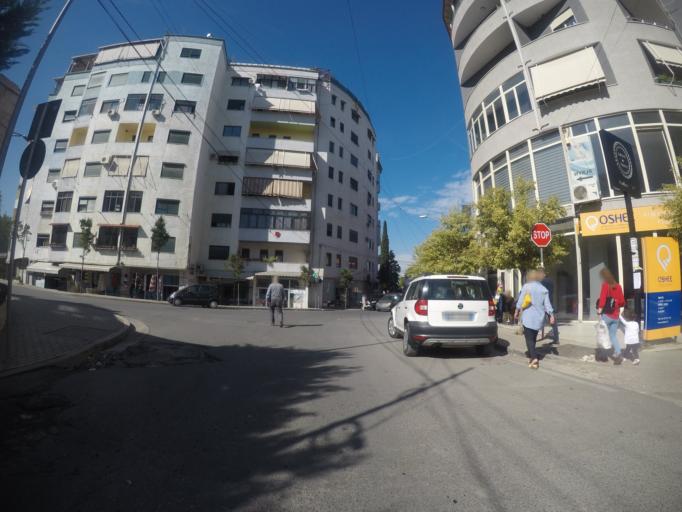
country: AL
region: Tirane
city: Tirana
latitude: 41.3460
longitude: 19.8562
